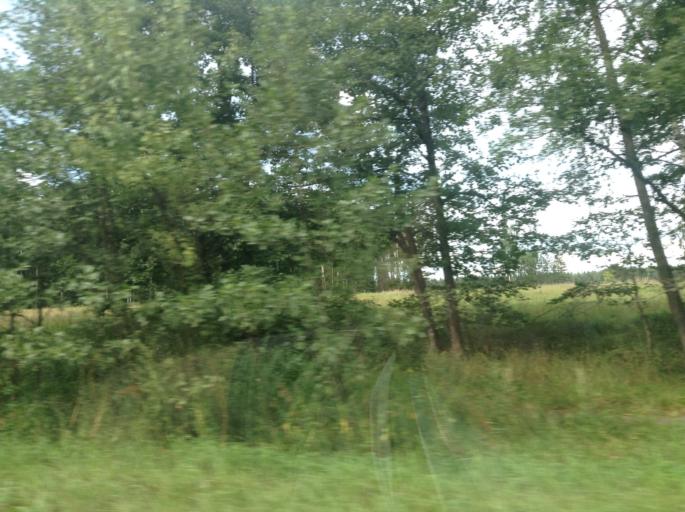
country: RU
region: Moskovskaya
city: Yegor'yevsk
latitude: 55.3585
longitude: 39.1153
